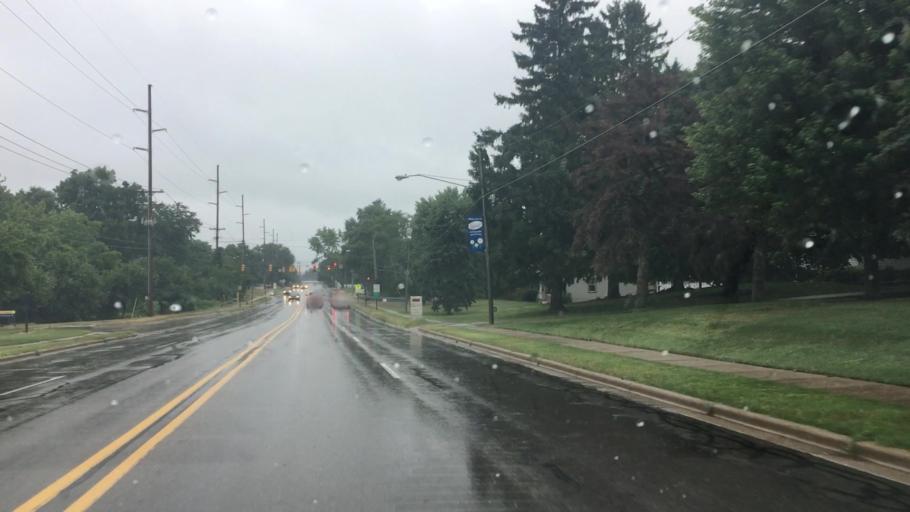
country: US
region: Michigan
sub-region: Ottawa County
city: Hudsonville
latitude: 42.8624
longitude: -85.8611
